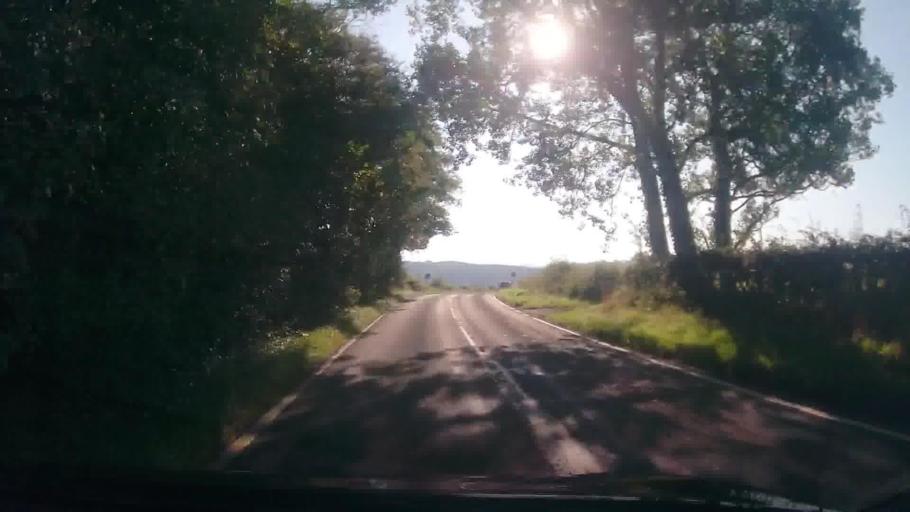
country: GB
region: England
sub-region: Cumbria
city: Seascale
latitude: 54.3746
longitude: -3.4114
